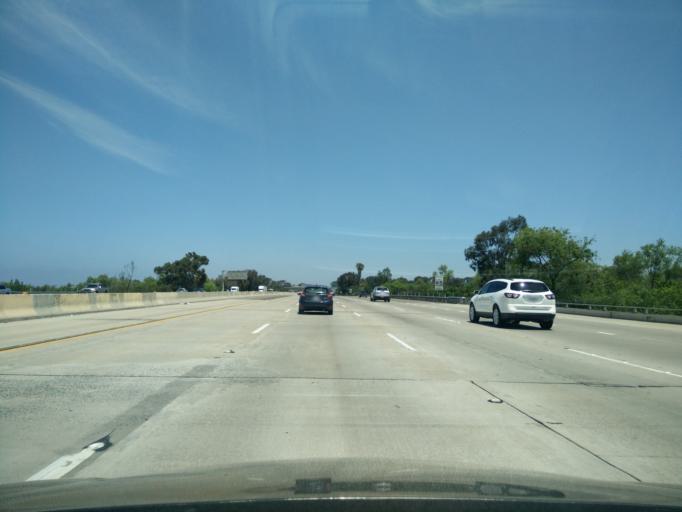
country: US
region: California
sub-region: San Diego County
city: Imperial Beach
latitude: 32.5891
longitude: -117.0878
